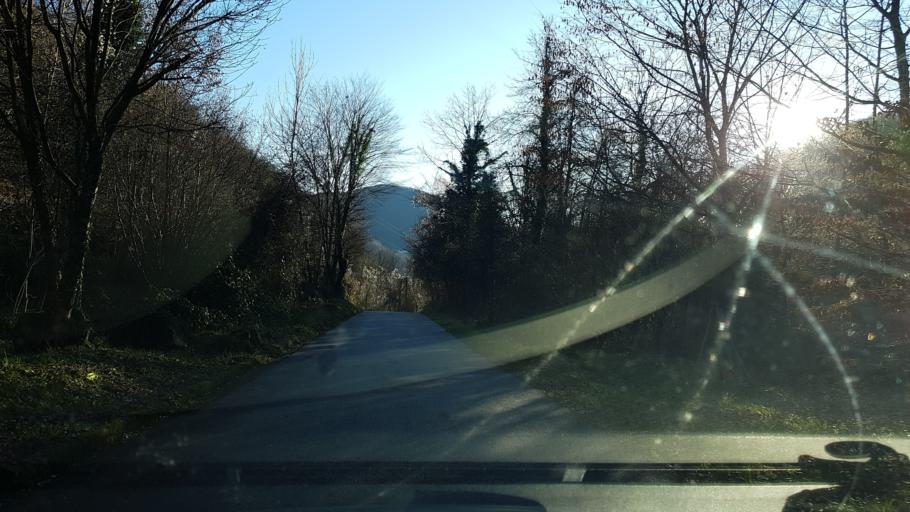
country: IT
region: Friuli Venezia Giulia
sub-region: Provincia di Udine
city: Savogna
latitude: 46.1715
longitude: 13.5367
